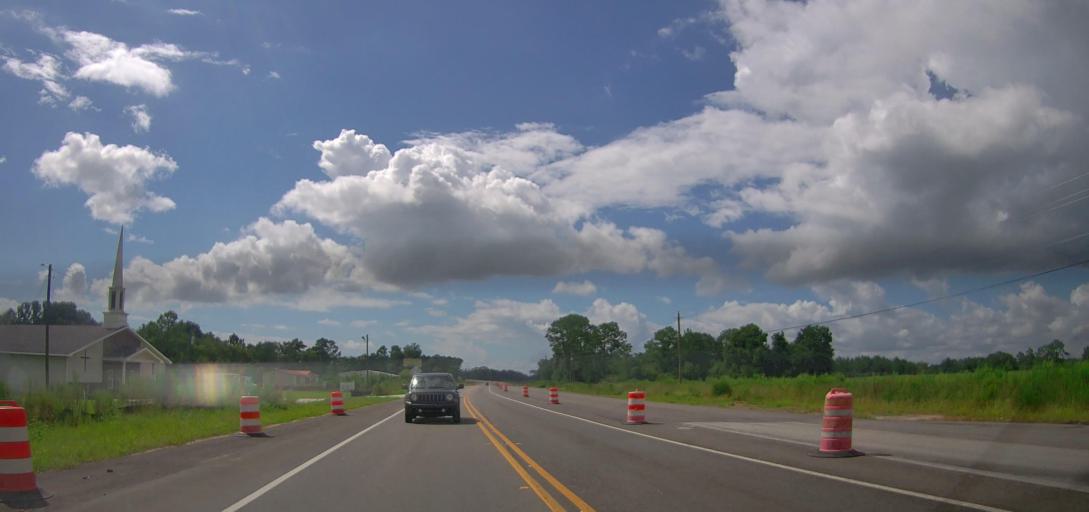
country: US
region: Georgia
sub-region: Coffee County
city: Douglas
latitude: 31.5435
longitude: -82.9311
